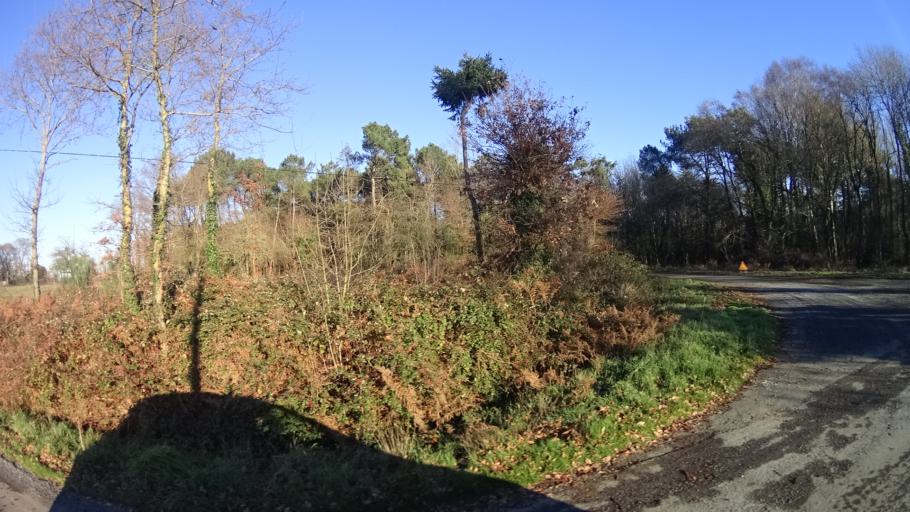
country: FR
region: Brittany
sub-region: Departement du Morbihan
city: Saint-Jacut-les-Pins
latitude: 47.6670
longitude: -2.1928
